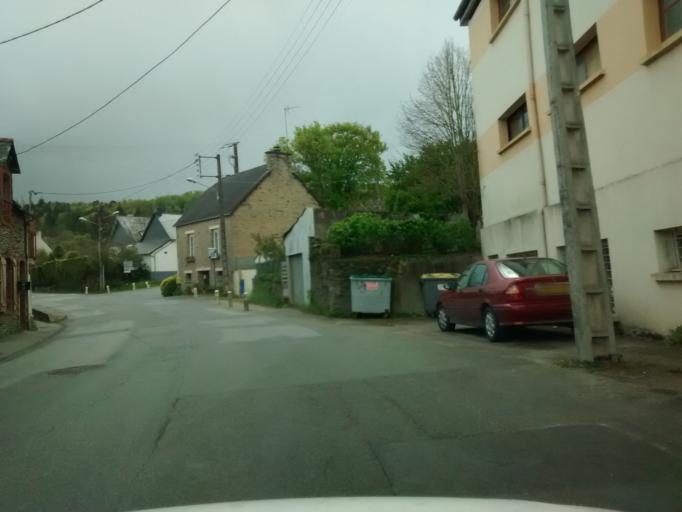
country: FR
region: Brittany
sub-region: Departement du Morbihan
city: Malestroit
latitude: 47.8064
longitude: -2.3805
